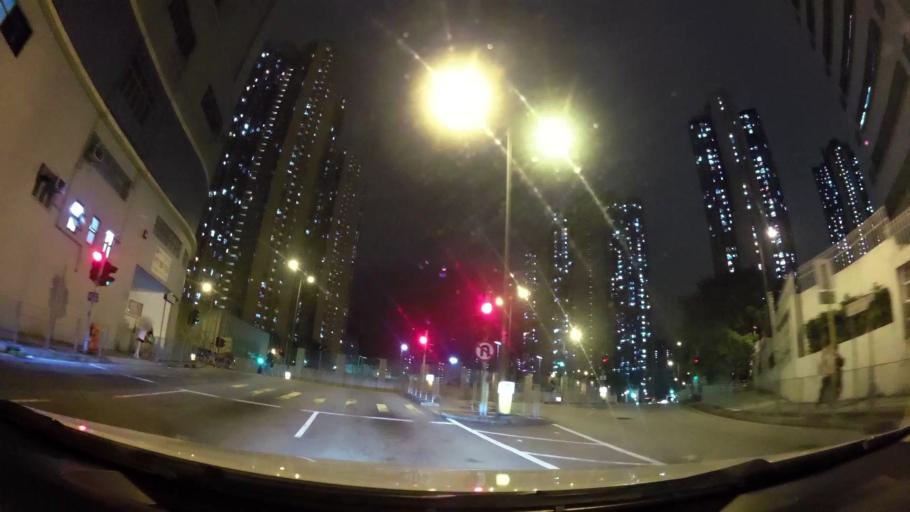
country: HK
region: Tsuen Wan
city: Tsuen Wan
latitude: 22.3693
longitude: 114.1293
